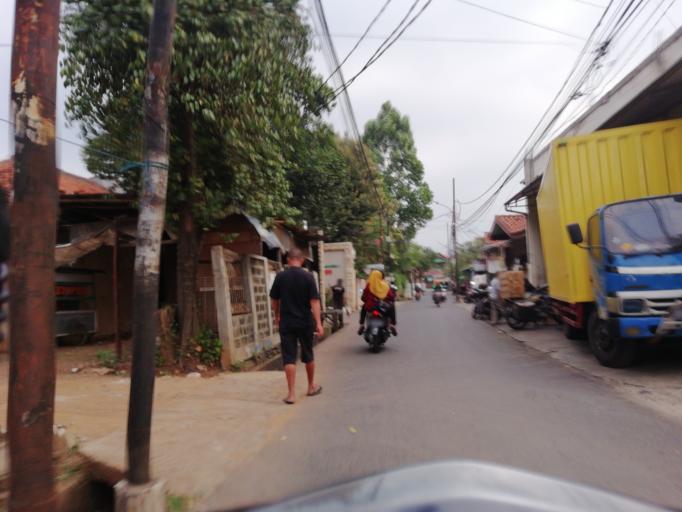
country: ID
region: West Java
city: Depok
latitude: -6.3287
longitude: 106.8201
